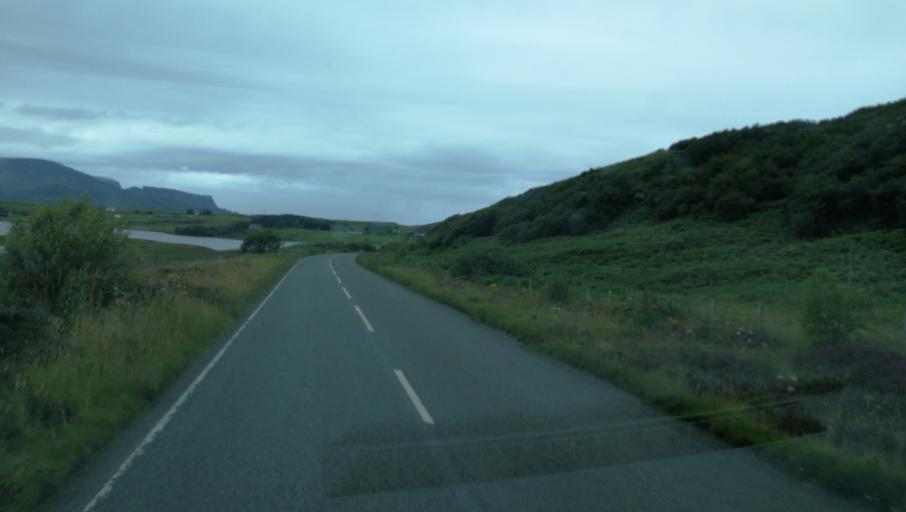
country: GB
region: Scotland
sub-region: Highland
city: Portree
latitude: 57.6037
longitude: -6.1690
